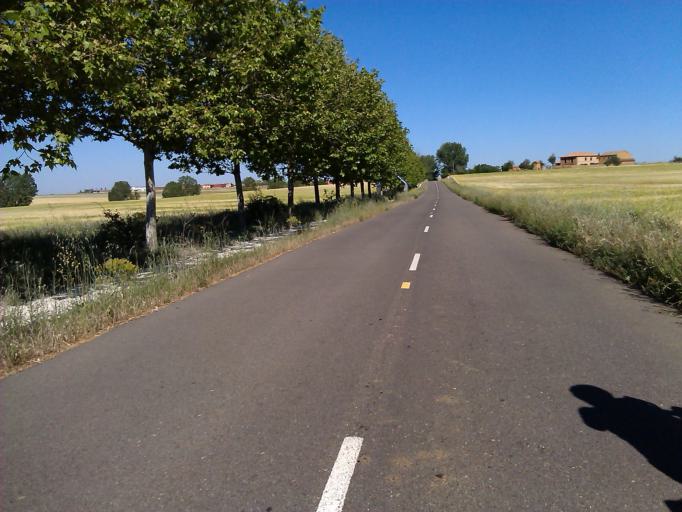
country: ES
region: Castille and Leon
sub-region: Provincia de Leon
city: Bercianos del Real Camino
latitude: 42.3883
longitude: -5.1264
